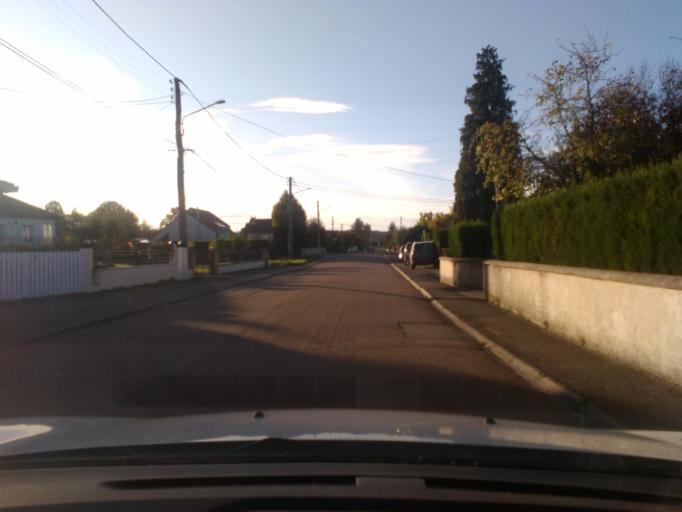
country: FR
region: Lorraine
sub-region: Departement des Vosges
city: Portieux
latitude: 48.3358
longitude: 6.3417
